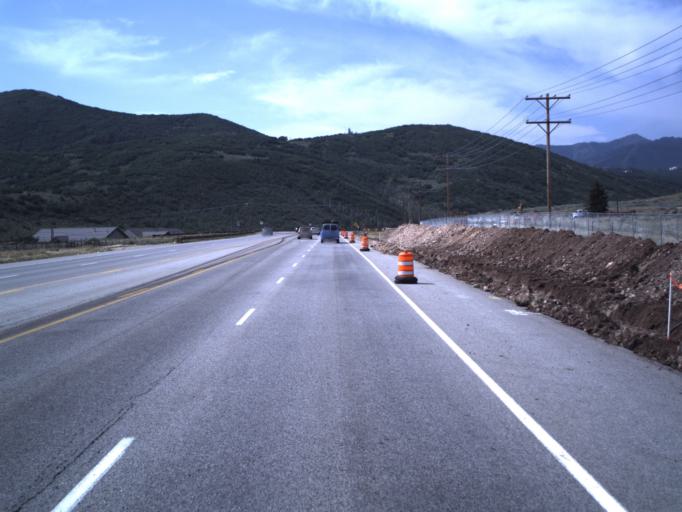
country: US
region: Utah
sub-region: Summit County
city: Park City
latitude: 40.6766
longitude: -111.4681
